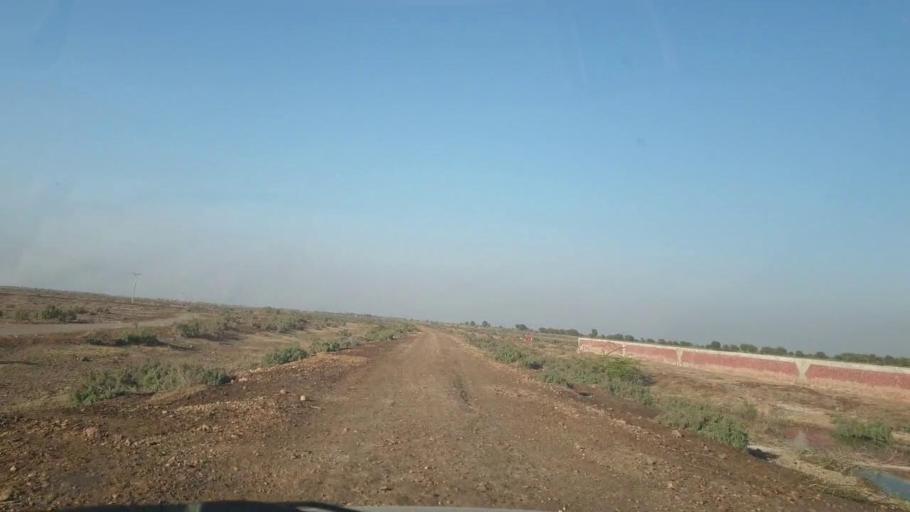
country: PK
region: Sindh
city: Mirpur Khas
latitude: 25.4334
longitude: 69.0993
